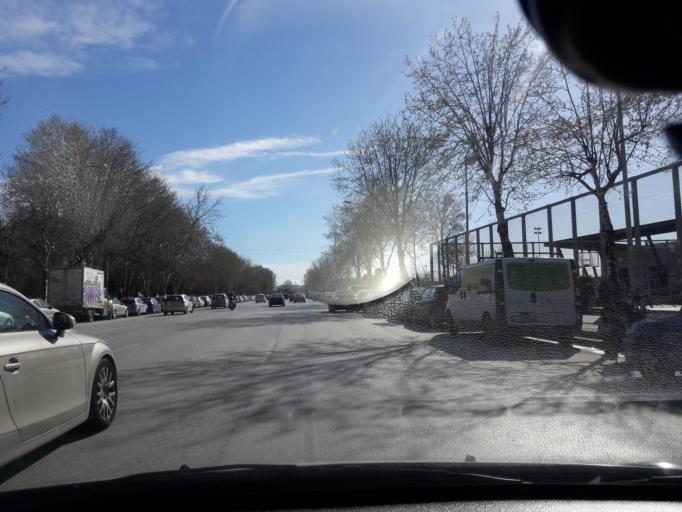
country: GR
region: Central Macedonia
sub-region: Nomos Thessalonikis
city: Kalamaria
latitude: 40.6060
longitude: 22.9508
